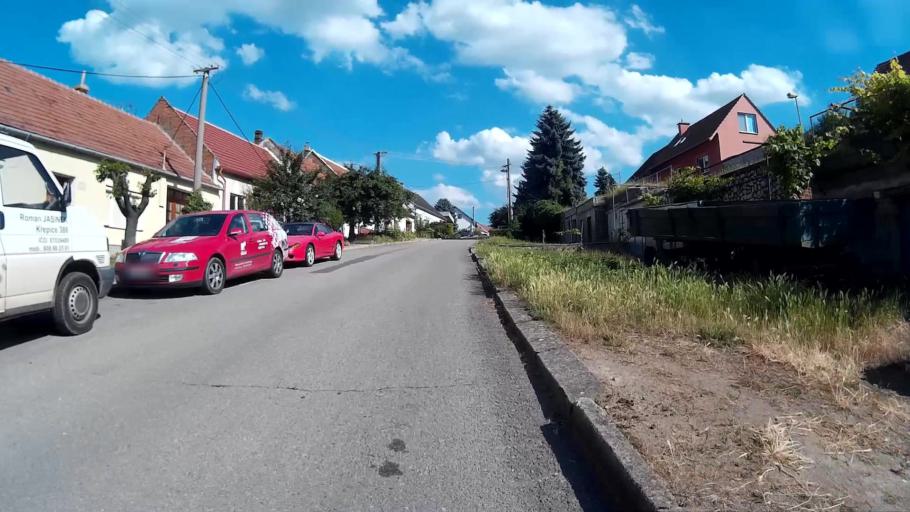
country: CZ
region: South Moravian
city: Krepice
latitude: 49.0007
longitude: 16.7188
